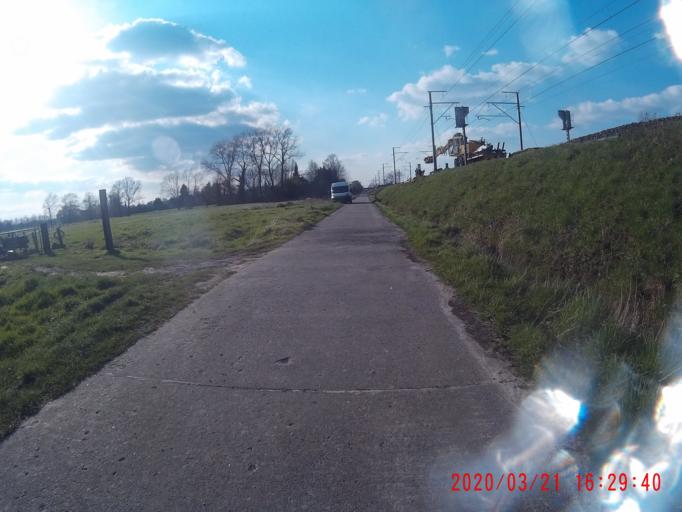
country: BE
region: Flanders
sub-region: Provincie Oost-Vlaanderen
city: Aalter
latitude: 51.0874
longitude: 3.4703
